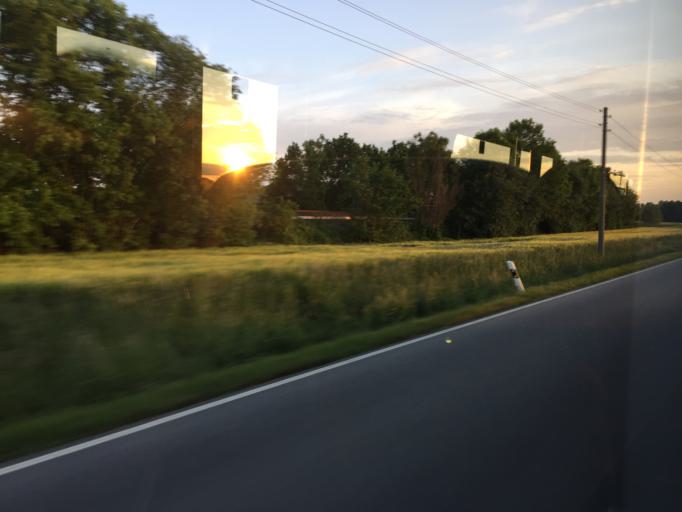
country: DE
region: Saxony
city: Sohland am Rotstein
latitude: 51.1192
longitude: 14.7272
